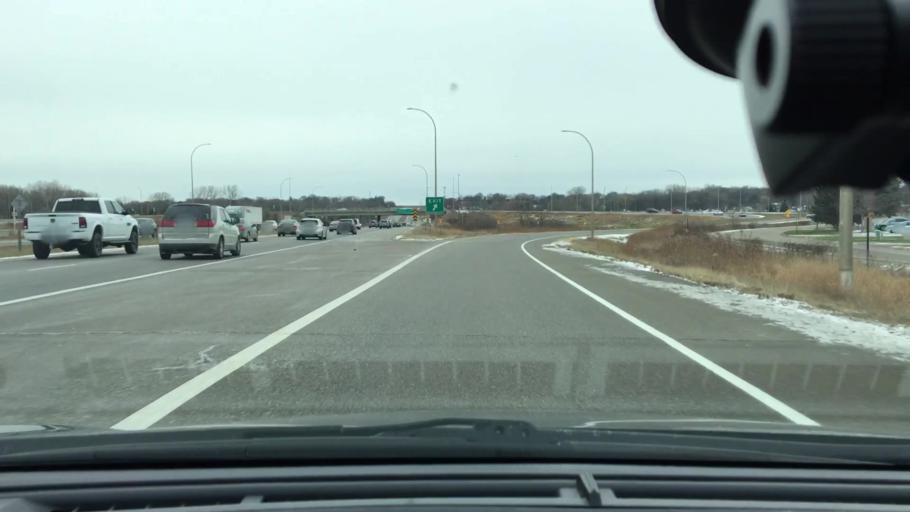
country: US
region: Minnesota
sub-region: Hennepin County
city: New Hope
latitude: 45.0367
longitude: -93.4010
